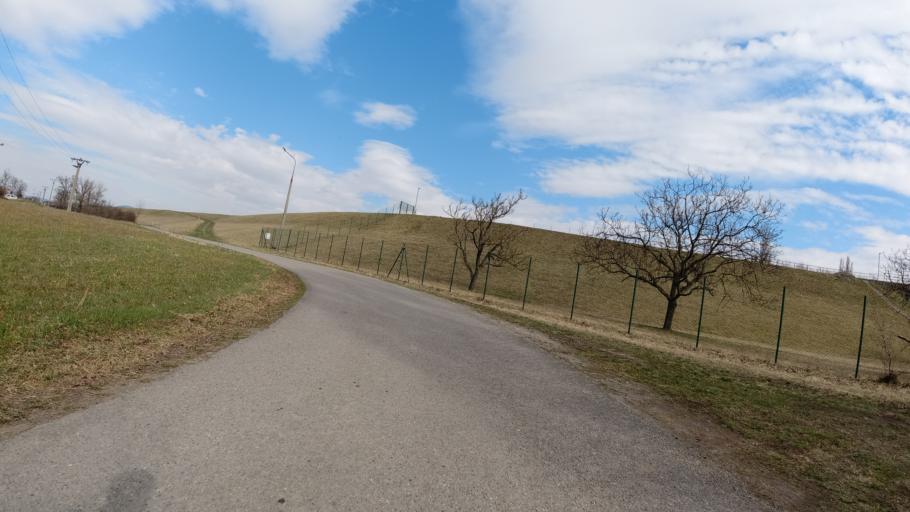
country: SK
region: Trnavsky
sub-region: Okres Trnava
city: Piestany
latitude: 48.6612
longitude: 17.8543
